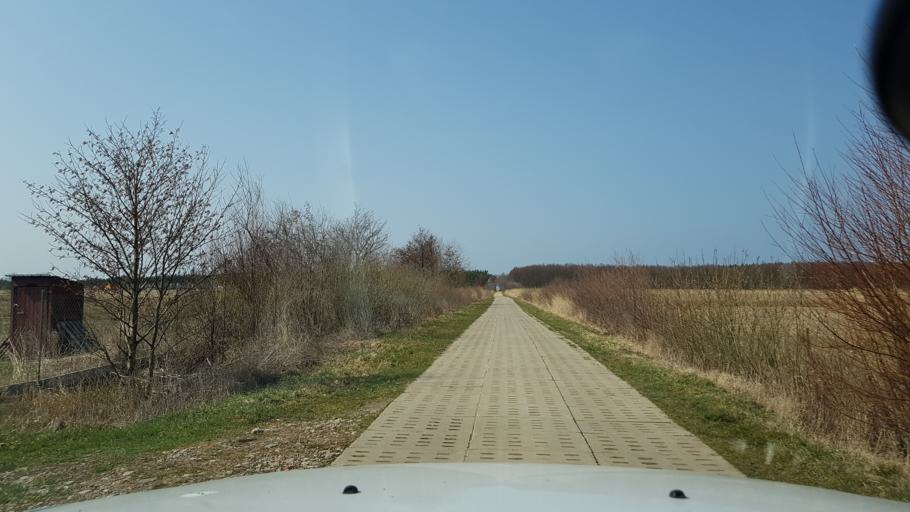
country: PL
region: West Pomeranian Voivodeship
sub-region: Powiat slawienski
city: Darlowo
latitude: 54.4616
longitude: 16.4207
